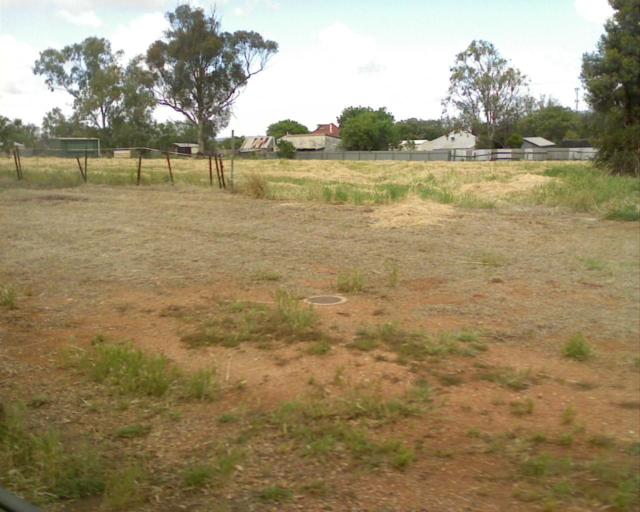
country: AU
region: South Australia
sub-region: Port Pirie City and Dists
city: Solomontown
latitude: -33.0318
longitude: 138.2717
